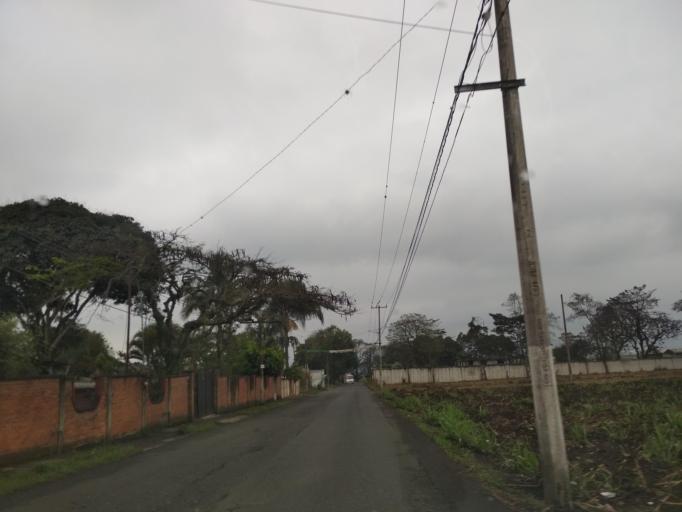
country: MX
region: Veracruz
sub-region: Cordoba
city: Veinte de Noviembre
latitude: 18.8617
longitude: -96.9529
